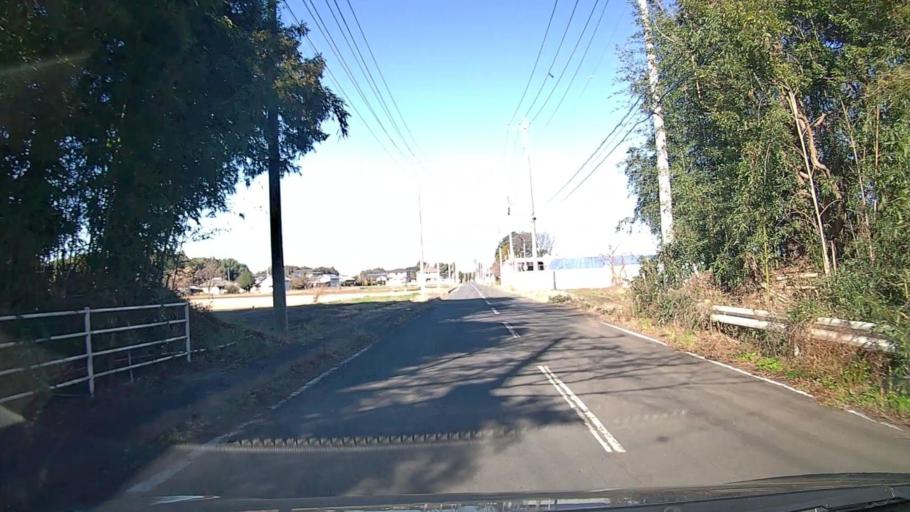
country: JP
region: Ibaraki
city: Mito-shi
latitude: 36.4404
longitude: 140.4417
